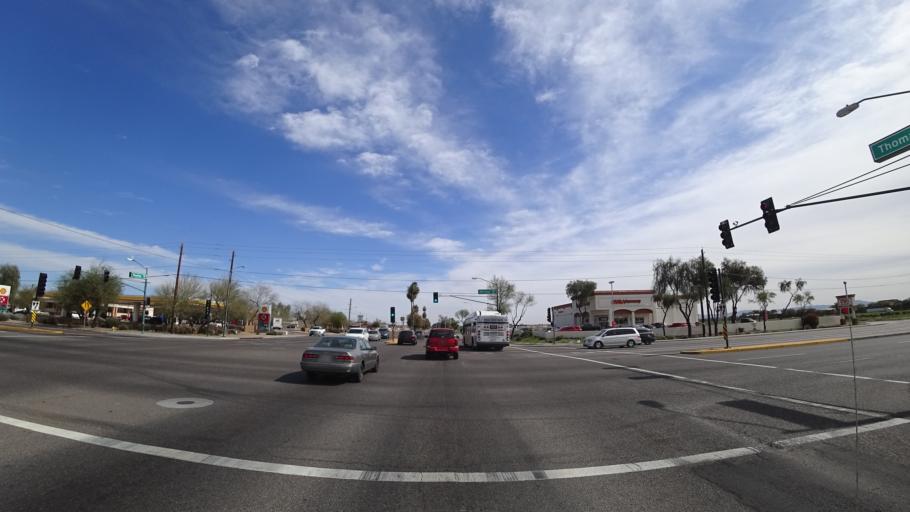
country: US
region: Arizona
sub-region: Maricopa County
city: Tolleson
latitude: 33.4797
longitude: -112.2382
